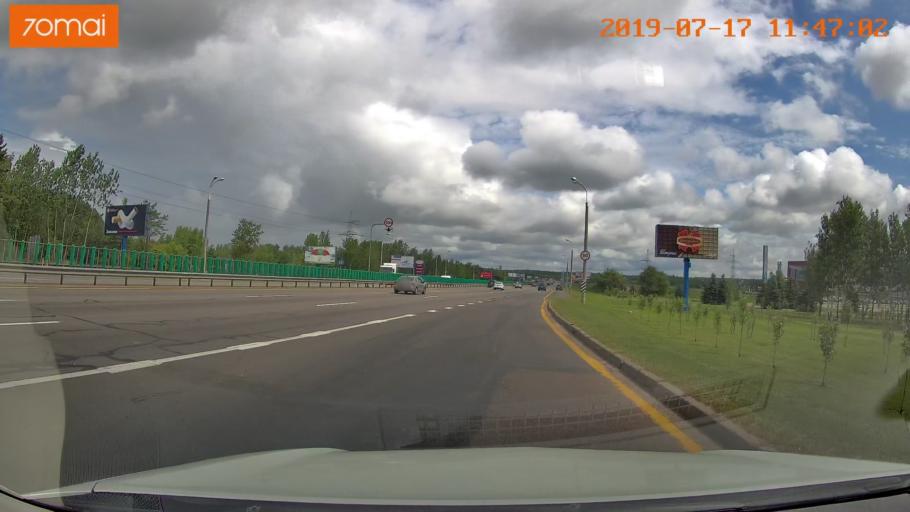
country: BY
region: Minsk
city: Zhdanovichy
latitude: 53.9524
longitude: 27.4482
